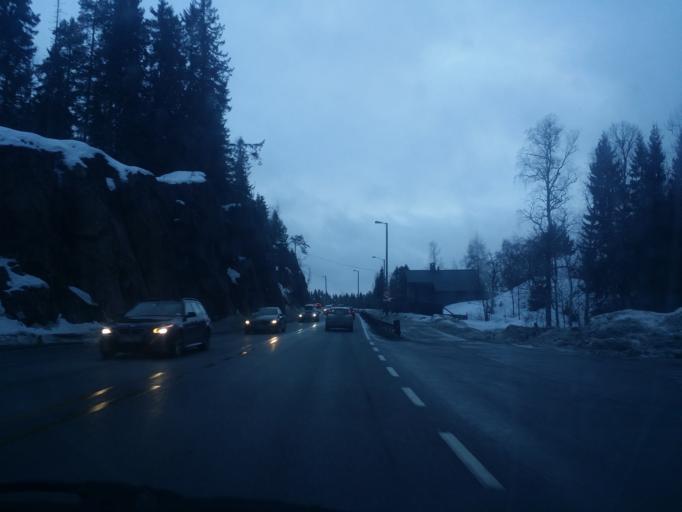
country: NO
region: Akershus
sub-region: Baerum
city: Skui
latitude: 59.9671
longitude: 10.3411
